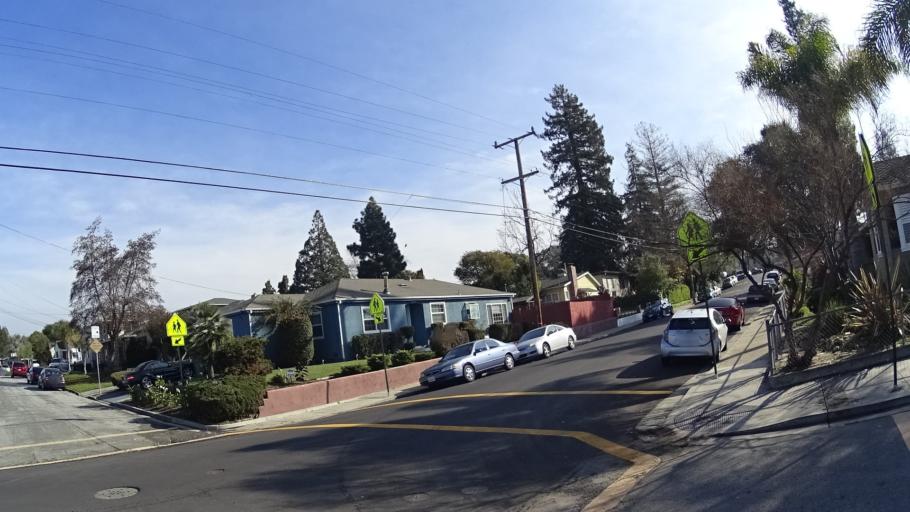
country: US
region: California
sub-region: Alameda County
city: Hayward
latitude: 37.6774
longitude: -122.0714
